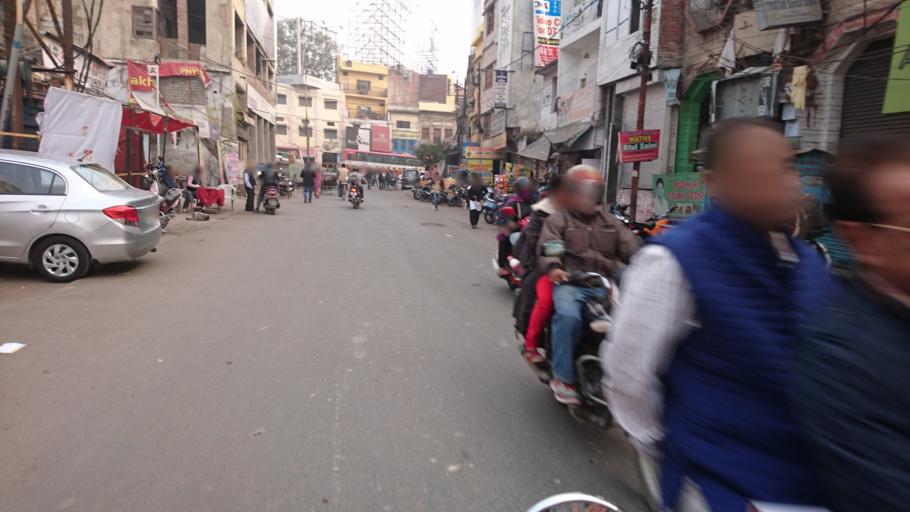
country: IN
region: Uttar Pradesh
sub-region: Lucknow District
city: Lucknow
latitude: 26.8481
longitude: 80.9464
